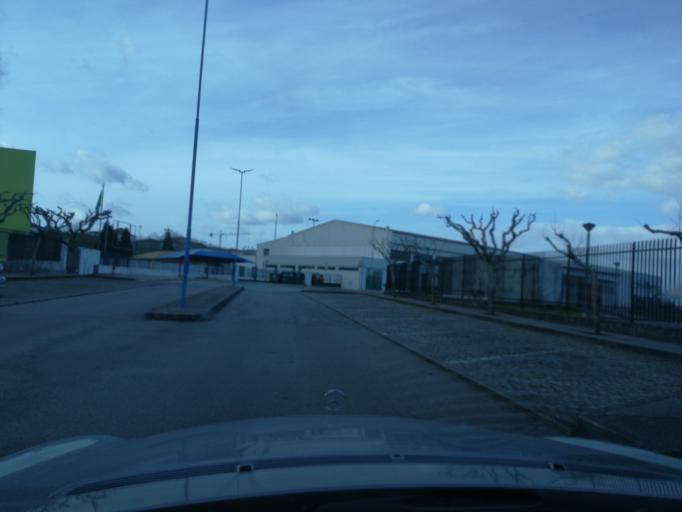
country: PT
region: Viana do Castelo
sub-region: Valenca
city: Valenza
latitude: 42.0289
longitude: -8.6391
